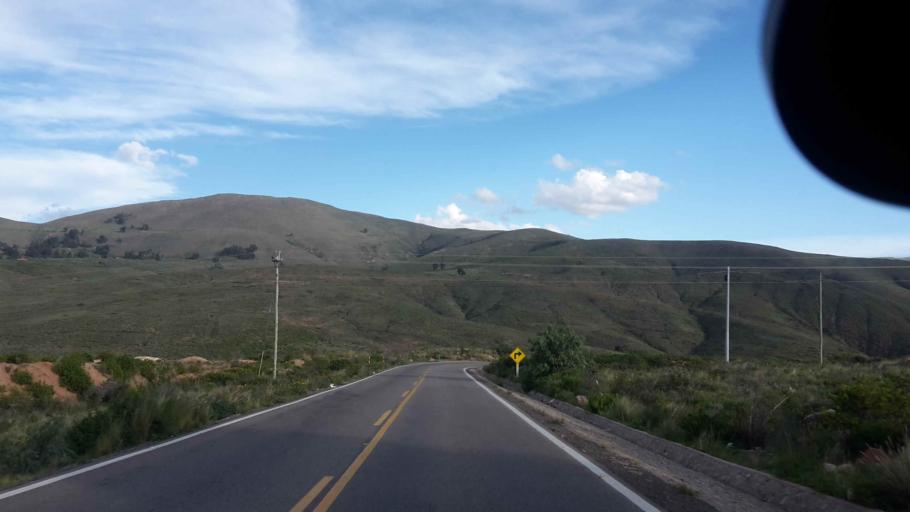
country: BO
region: Cochabamba
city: Arani
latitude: -17.5740
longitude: -65.7286
